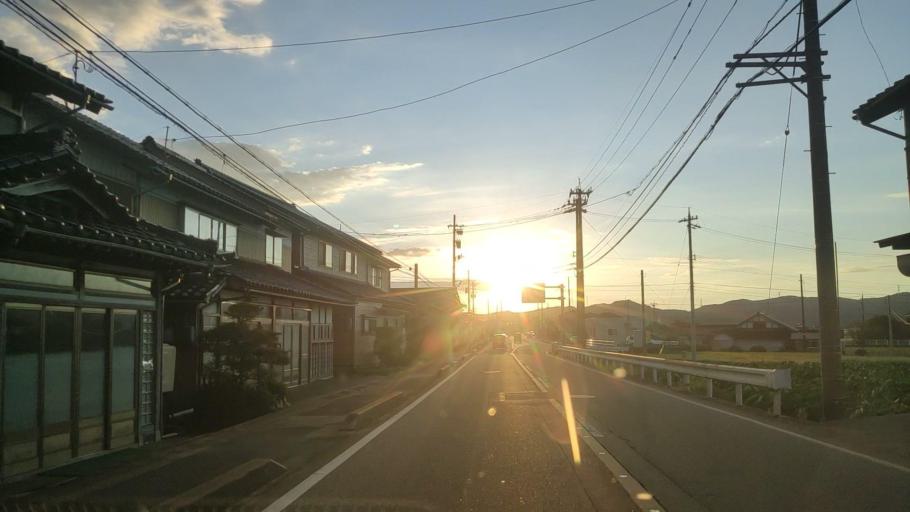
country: JP
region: Toyama
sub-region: Oyabe Shi
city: Oyabe
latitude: 36.6320
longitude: 136.8588
